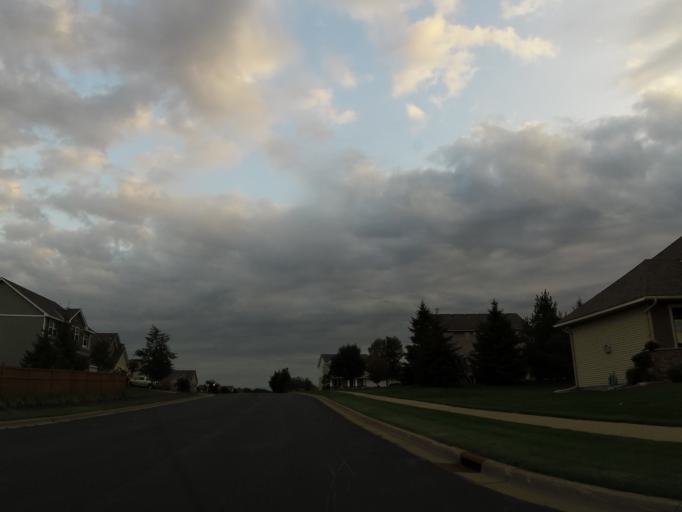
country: US
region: Minnesota
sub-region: Scott County
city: Prior Lake
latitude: 44.6961
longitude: -93.4526
